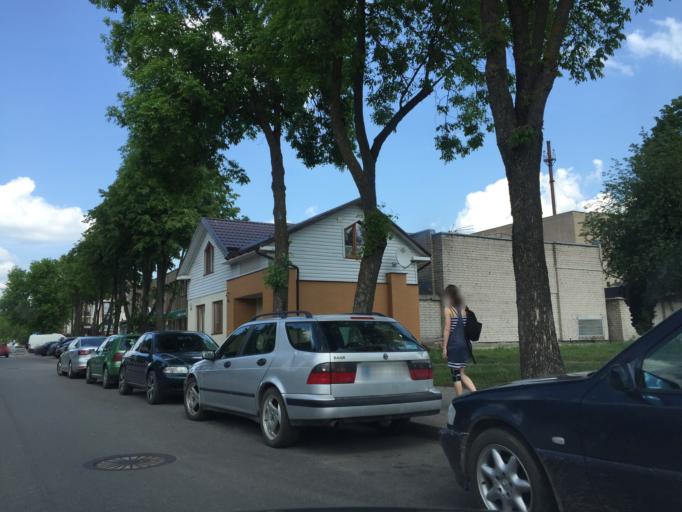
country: LT
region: Klaipedos apskritis
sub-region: Klaipeda
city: Palanga
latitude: 55.9185
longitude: 21.0721
